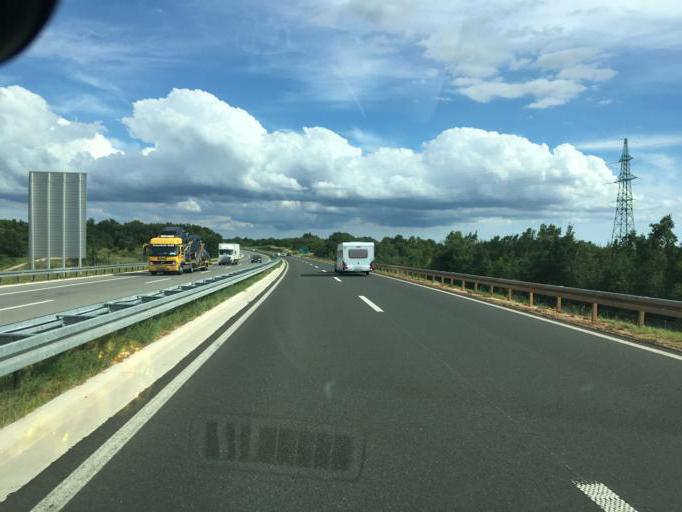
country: HR
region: Istarska
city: Vodnjan
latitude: 45.0993
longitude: 13.8196
